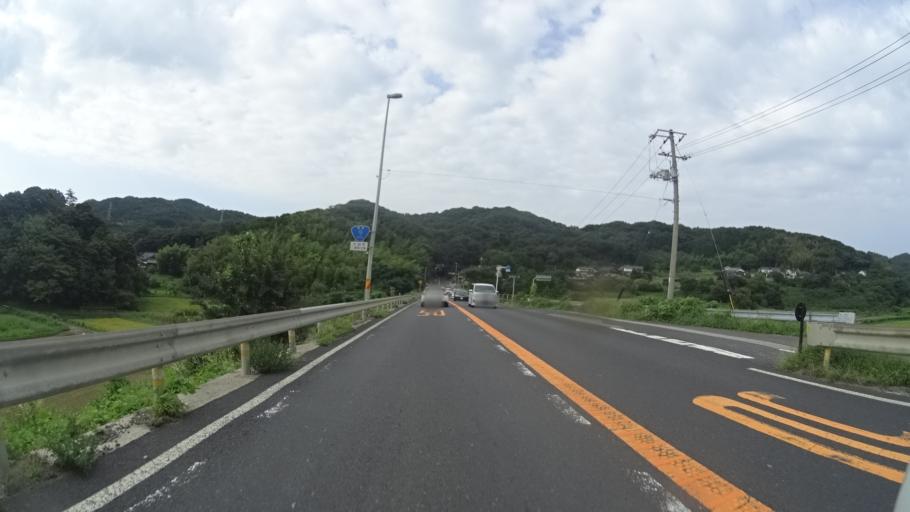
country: JP
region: Shimane
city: Odacho-oda
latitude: 35.1623
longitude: 132.4141
